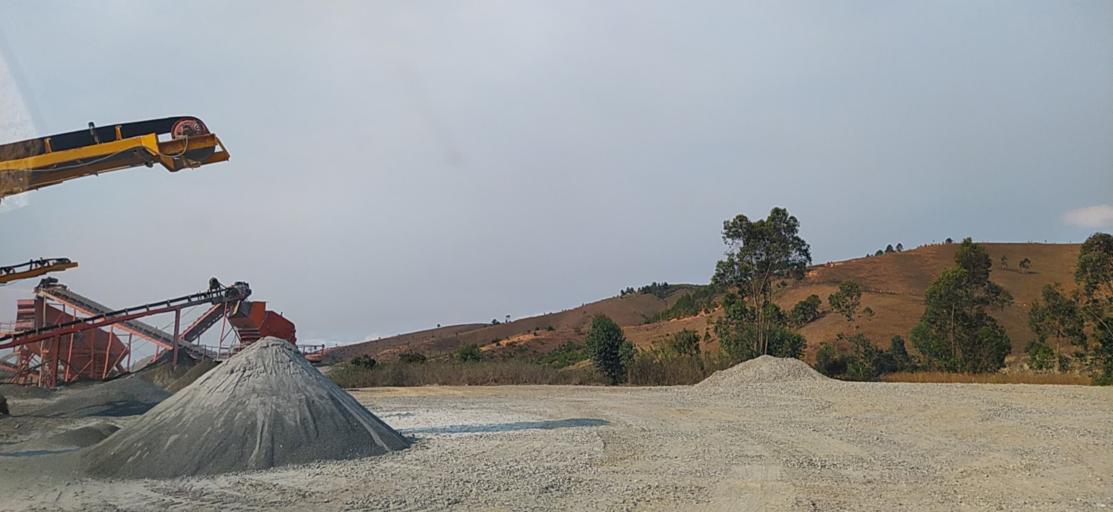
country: MG
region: Alaotra Mangoro
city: Moramanga
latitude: -18.6702
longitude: 48.2750
